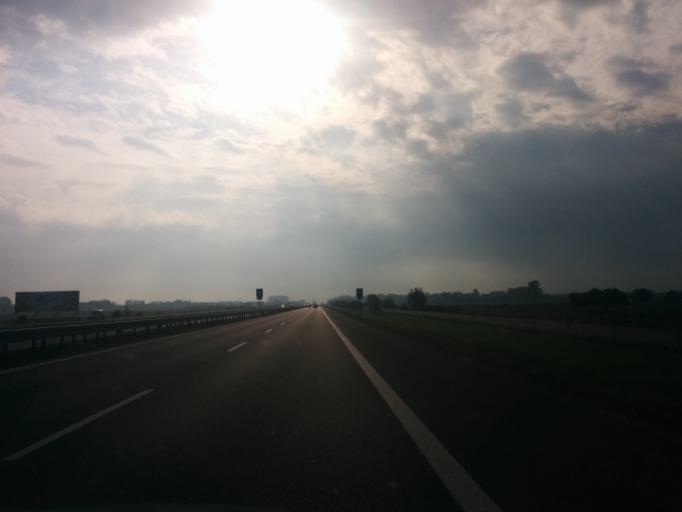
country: PL
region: Masovian Voivodeship
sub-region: Powiat radomski
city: Jedlinsk
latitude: 51.5385
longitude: 21.0679
